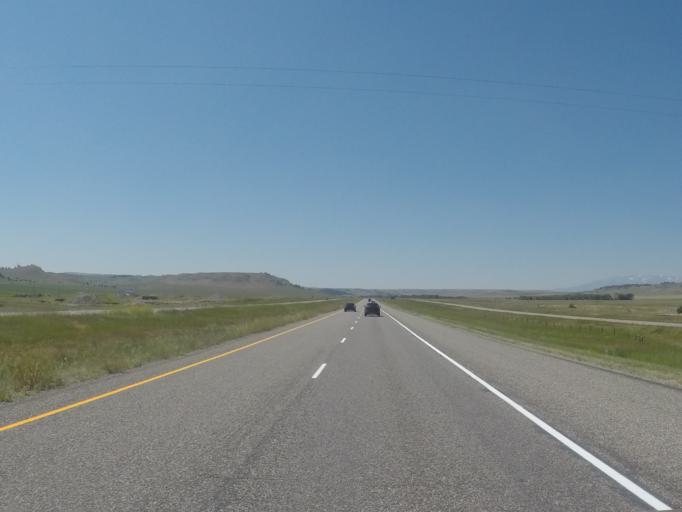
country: US
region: Montana
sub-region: Sweet Grass County
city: Big Timber
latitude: 45.7336
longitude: -109.6920
